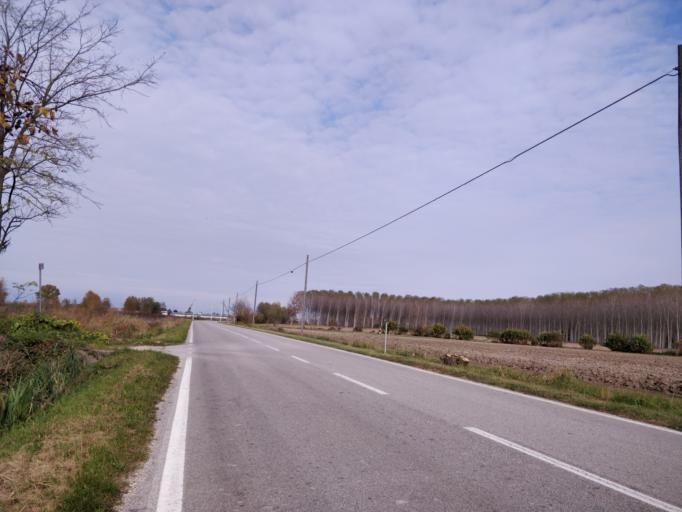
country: IT
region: Friuli Venezia Giulia
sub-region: Provincia di Udine
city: Bertiolo
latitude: 45.9270
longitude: 13.0485
